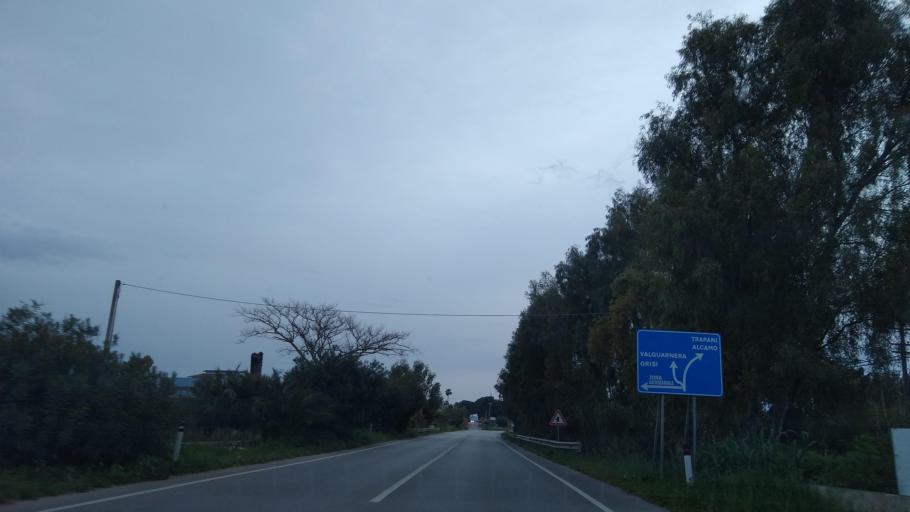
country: IT
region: Sicily
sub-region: Palermo
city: Partinico
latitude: 38.0298
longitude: 13.0932
